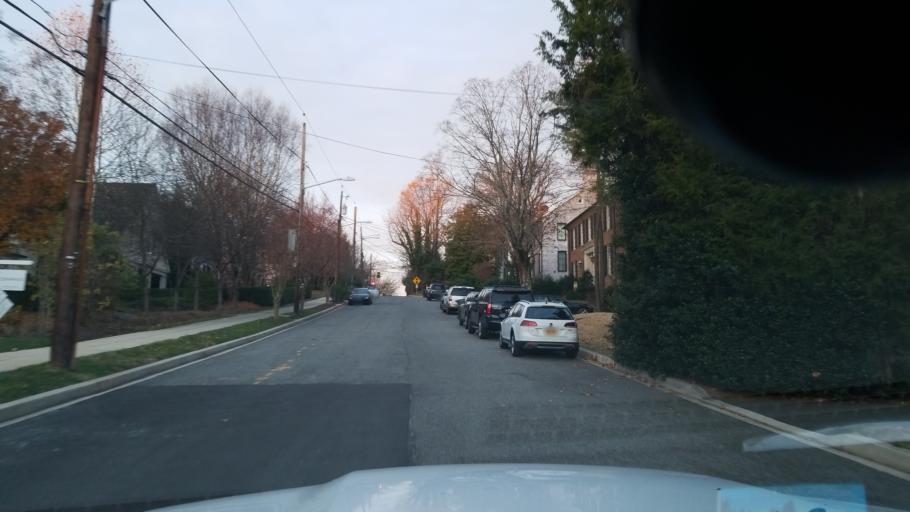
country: US
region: Maryland
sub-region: Montgomery County
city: Brookmont
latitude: 38.9192
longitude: -77.0869
